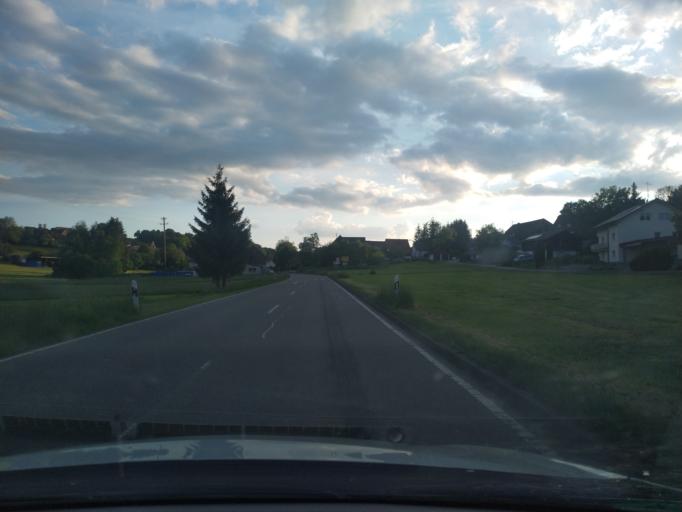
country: DE
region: Baden-Wuerttemberg
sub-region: Freiburg Region
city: Bonndorf im Schwarzwald
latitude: 47.8268
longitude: 8.4010
